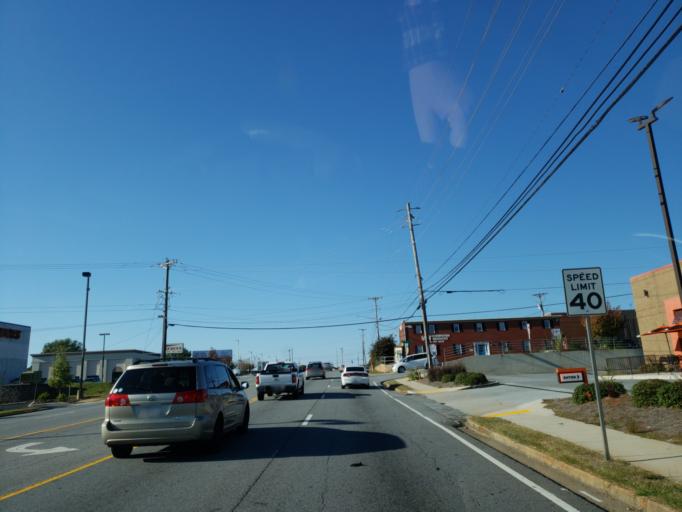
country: US
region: Georgia
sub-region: Gwinnett County
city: Lawrenceville
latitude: 33.9631
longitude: -84.0069
